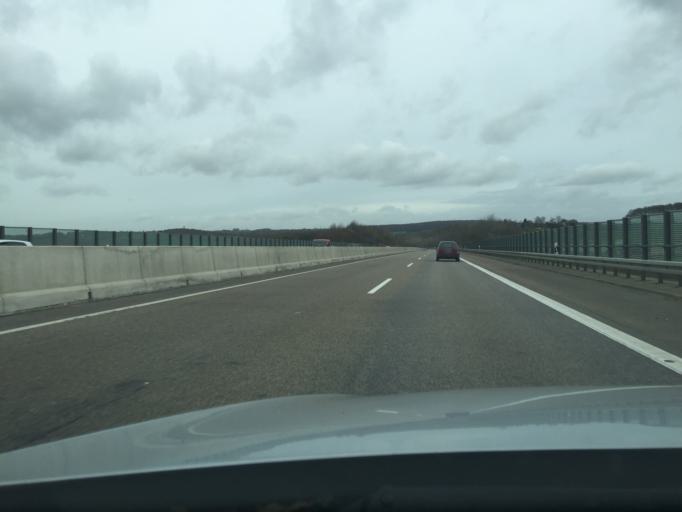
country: DE
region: North Rhine-Westphalia
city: Wulfrath
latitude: 51.2651
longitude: 7.0834
